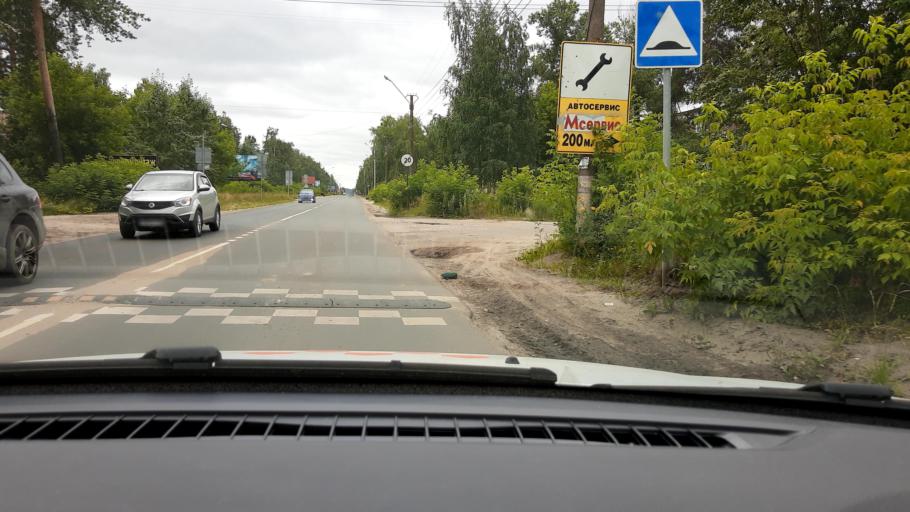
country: RU
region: Nizjnij Novgorod
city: Pyra
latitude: 56.2454
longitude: 43.3906
